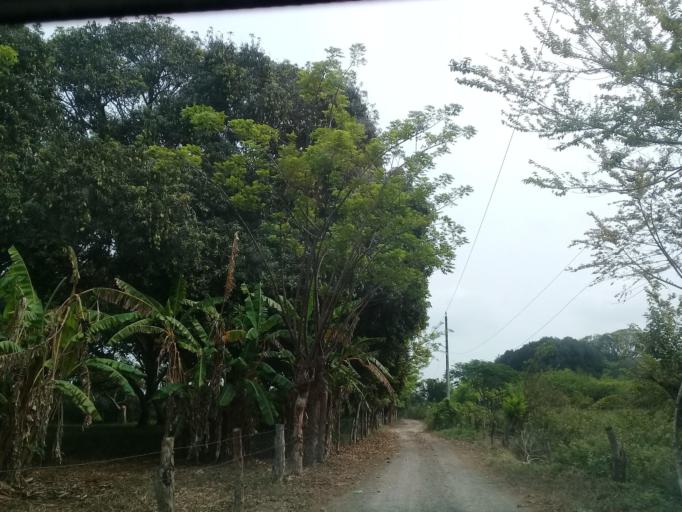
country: MX
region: Veracruz
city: El Tejar
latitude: 19.0561
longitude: -96.1918
